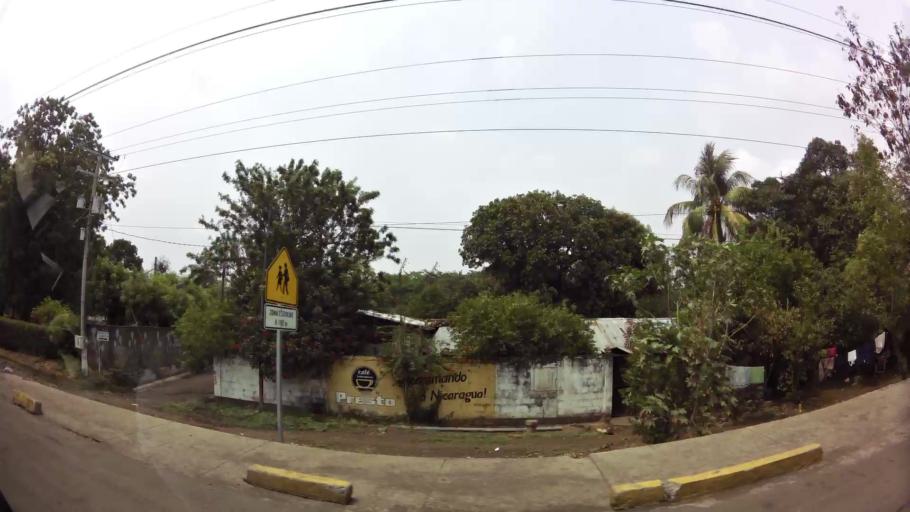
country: NI
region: Chinandega
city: Chinandega
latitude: 12.6368
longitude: -87.1211
